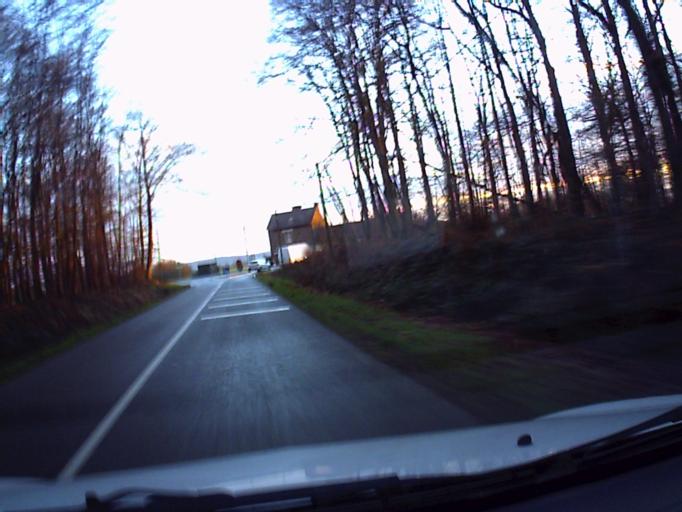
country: FR
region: Brittany
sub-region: Departement d'Ille-et-Vilaine
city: Iffendic
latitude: 48.1548
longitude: -2.0138
